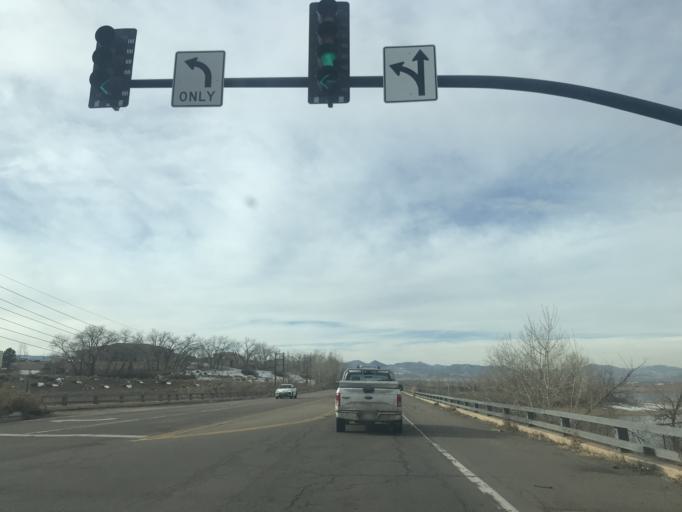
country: US
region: Colorado
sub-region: Arapahoe County
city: Columbine Valley
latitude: 39.5651
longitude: -105.0102
